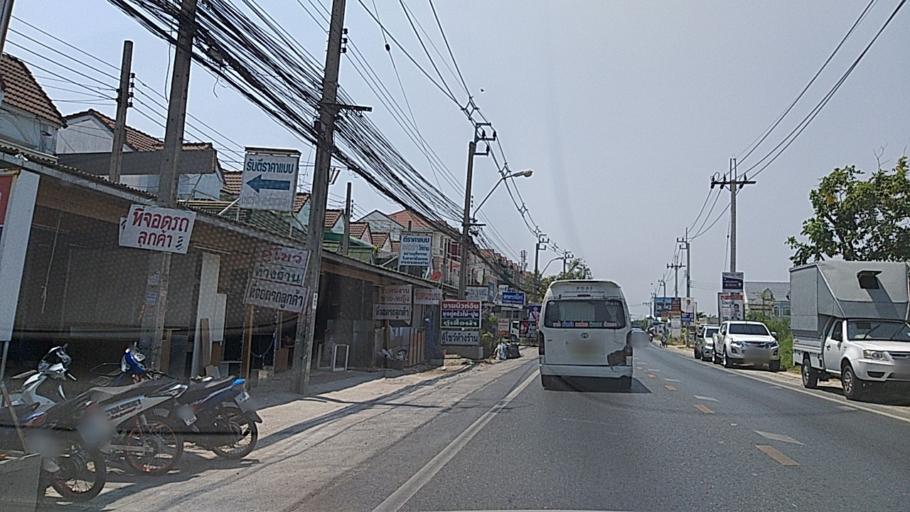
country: TH
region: Nonthaburi
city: Bang Bua Thong
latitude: 13.9159
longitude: 100.4005
